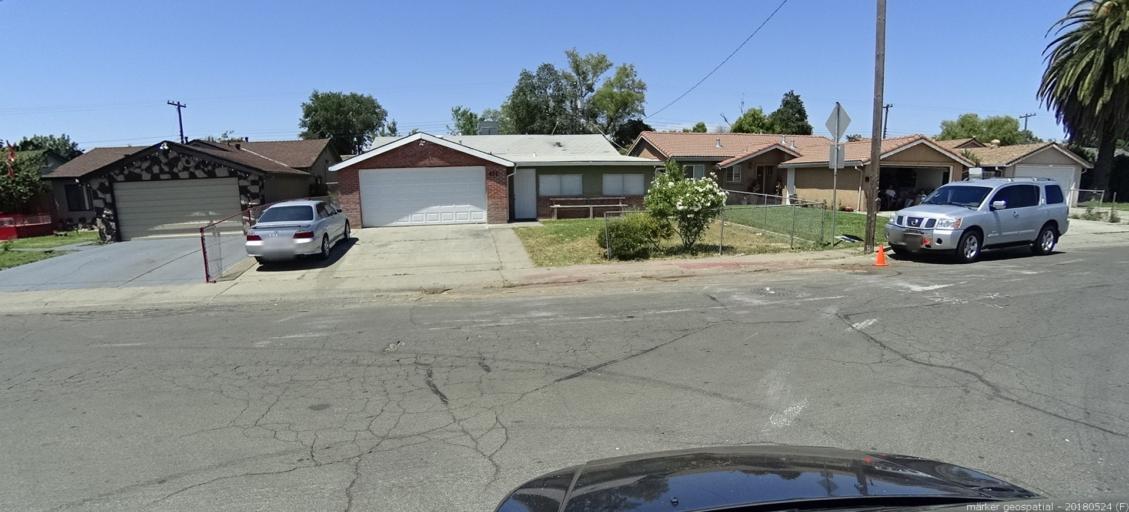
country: US
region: California
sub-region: Sacramento County
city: Sacramento
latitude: 38.6235
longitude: -121.4553
